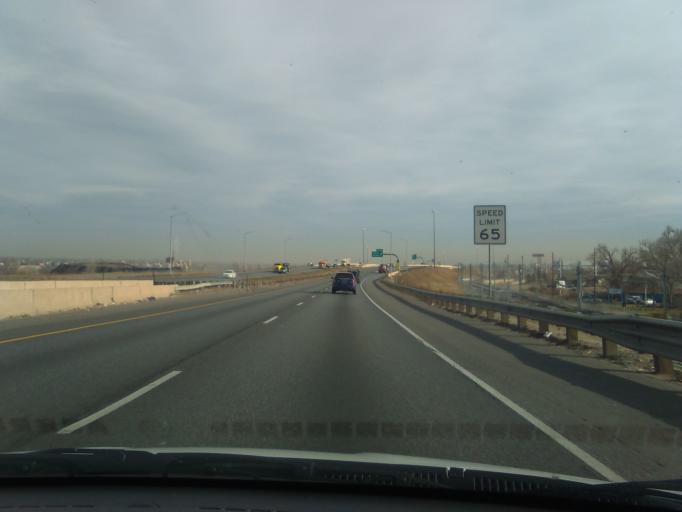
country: US
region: Colorado
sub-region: Adams County
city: Berkley
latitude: 39.8059
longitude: -105.0131
